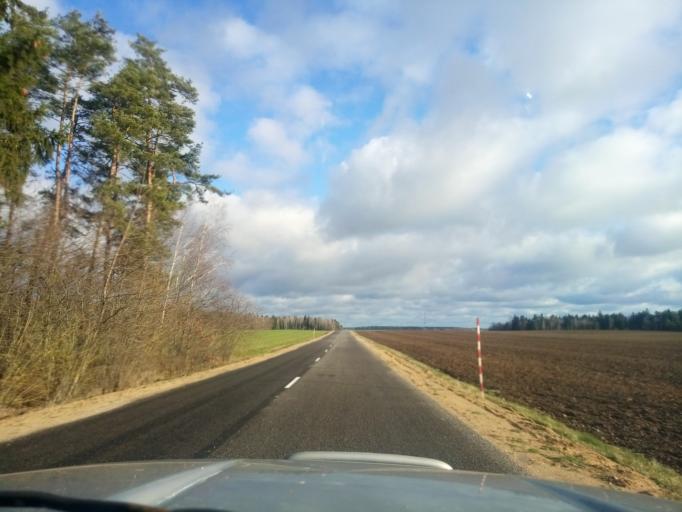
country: BY
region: Minsk
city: Tsimkavichy
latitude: 53.1370
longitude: 26.9959
